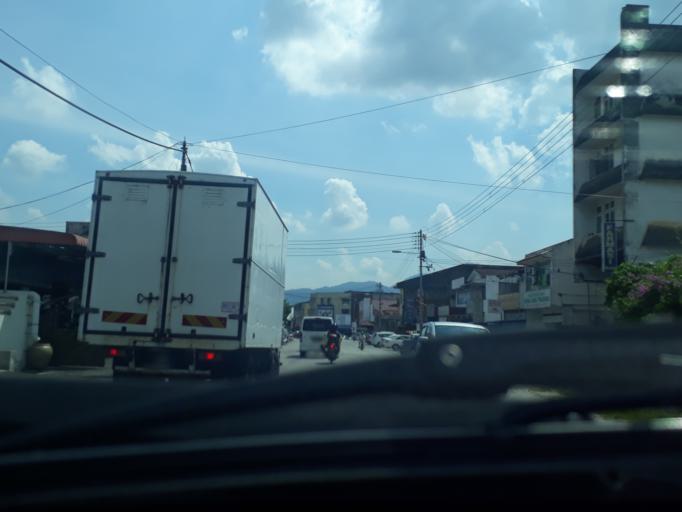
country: MY
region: Perak
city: Ipoh
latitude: 4.5822
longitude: 101.0841
